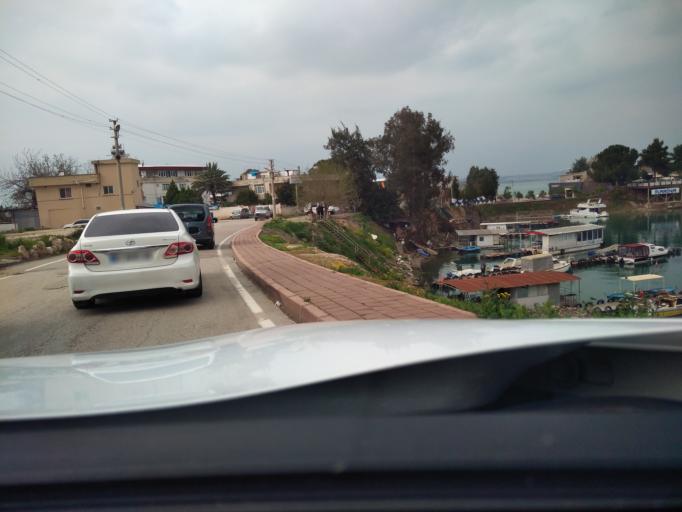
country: TR
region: Adana
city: Adana
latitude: 37.0628
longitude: 35.2994
